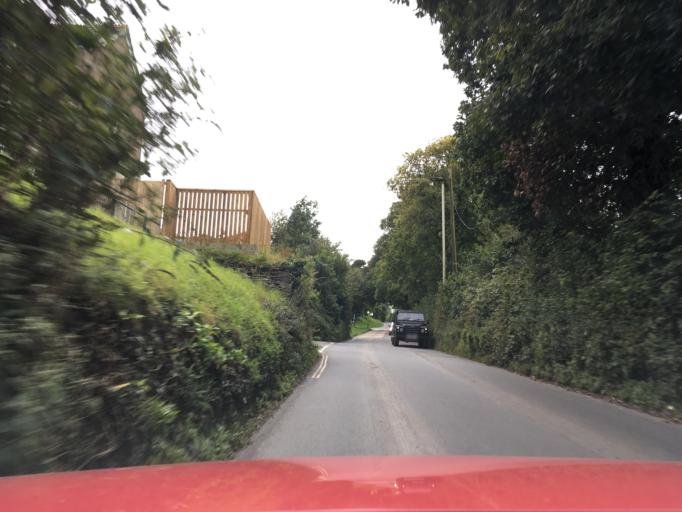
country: GB
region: England
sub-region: Devon
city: Kingsbridge
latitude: 50.2821
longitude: -3.7839
